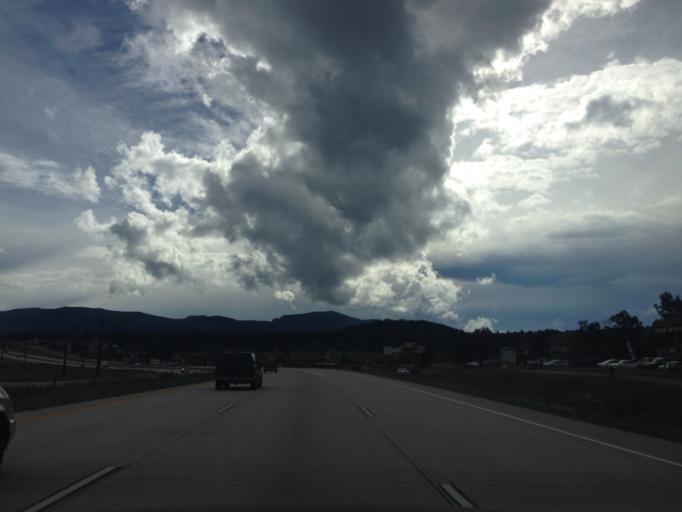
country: US
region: Colorado
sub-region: Jefferson County
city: Indian Hills
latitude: 39.5427
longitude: -105.2925
